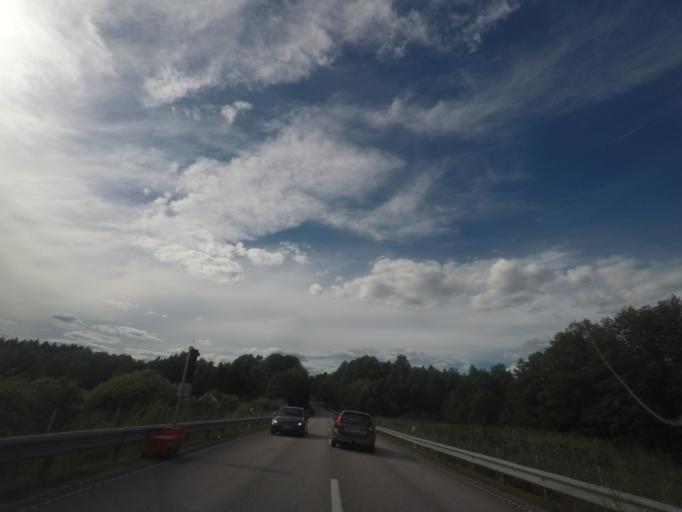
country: SE
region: Stockholm
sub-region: Norrtalje Kommun
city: Skanninge
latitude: 59.9033
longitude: 18.5893
